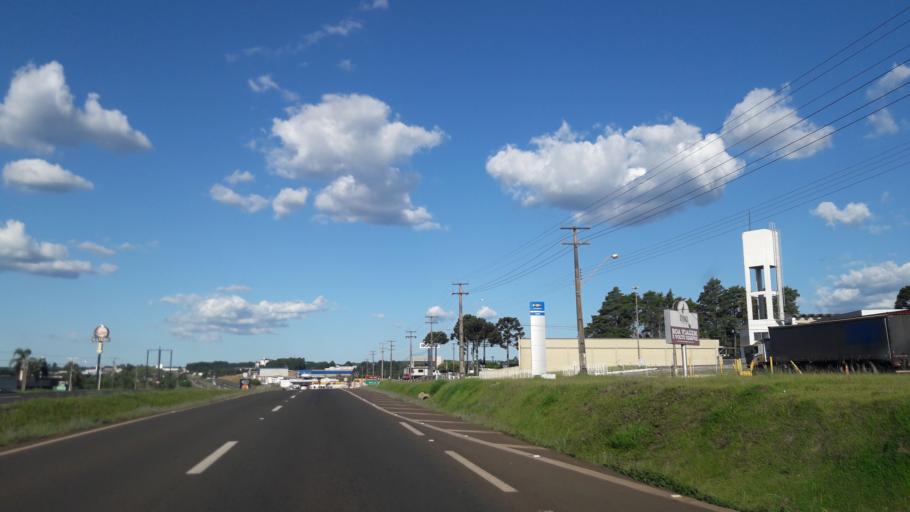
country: BR
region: Parana
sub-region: Guarapuava
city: Guarapuava
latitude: -25.3610
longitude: -51.4692
